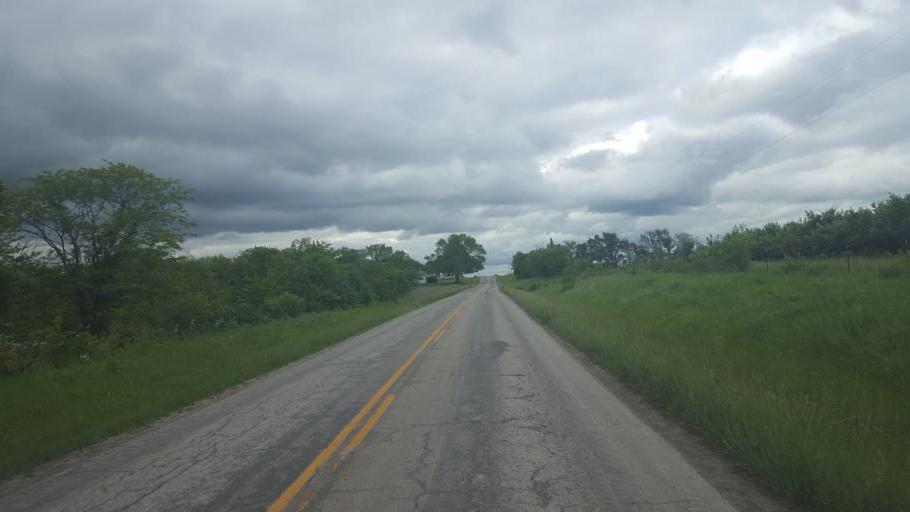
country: US
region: Missouri
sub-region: Mercer County
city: Princeton
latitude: 40.2546
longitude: -93.6757
